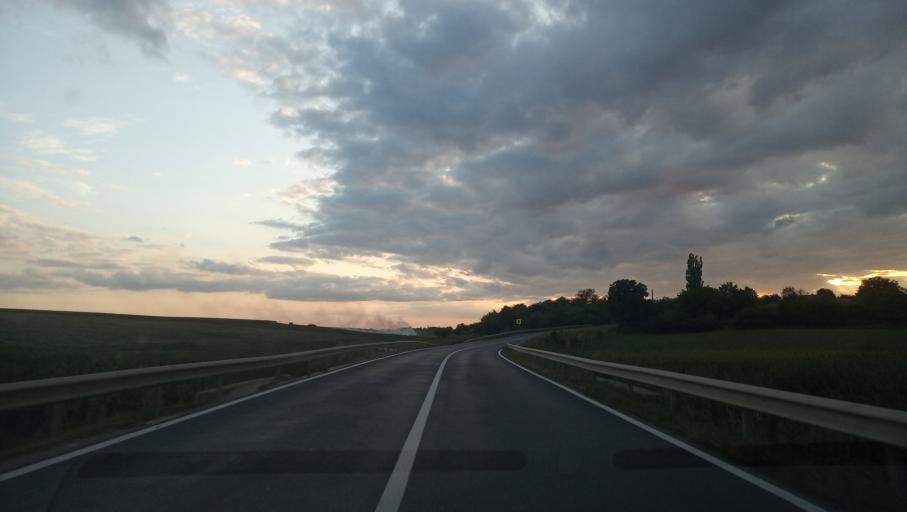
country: RO
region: Calarasi
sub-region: Comuna Vlad Tepes
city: Mihai Viteazu
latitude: 44.3623
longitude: 27.0085
